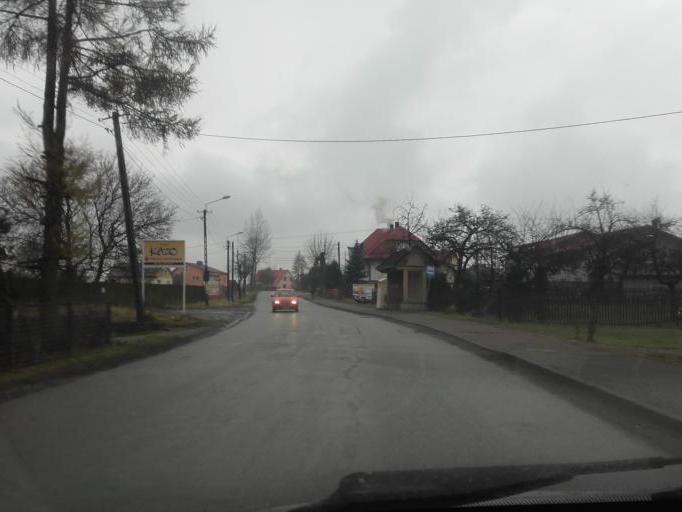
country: PL
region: Silesian Voivodeship
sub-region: Powiat cieszynski
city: Koniakow
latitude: 49.5491
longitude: 18.9341
